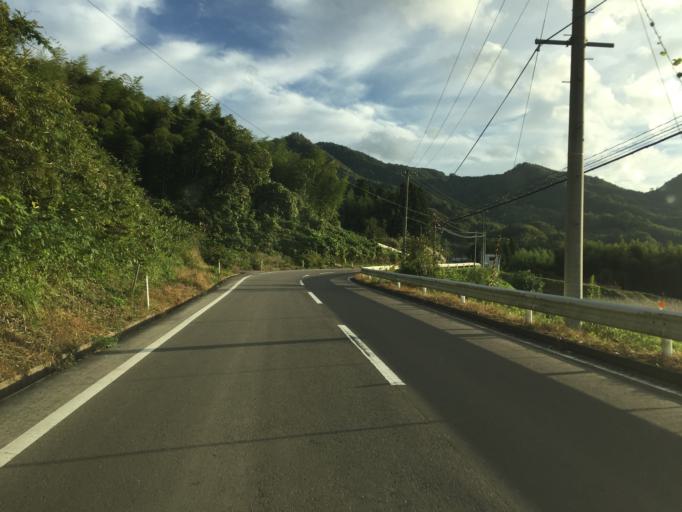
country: JP
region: Fukushima
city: Yanagawamachi-saiwaicho
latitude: 37.9041
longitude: 140.6630
